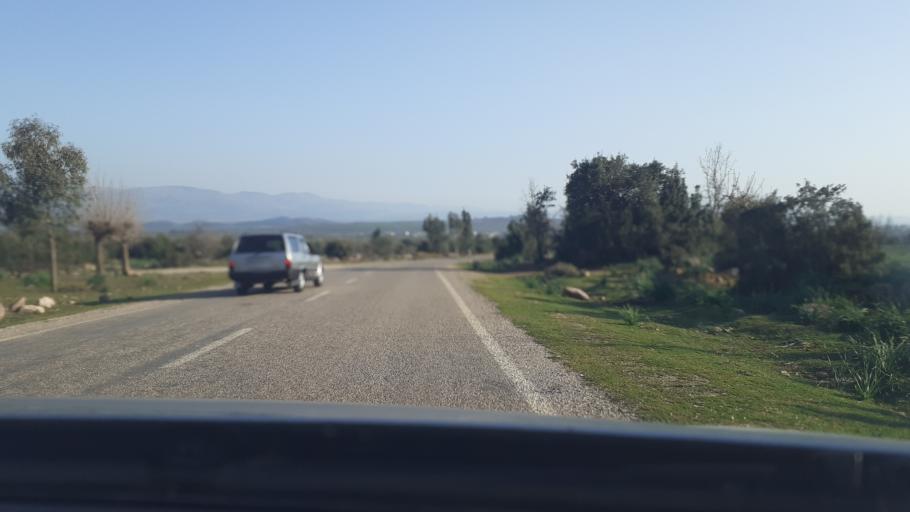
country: TR
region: Hatay
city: Aktepe
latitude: 36.7261
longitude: 36.4844
